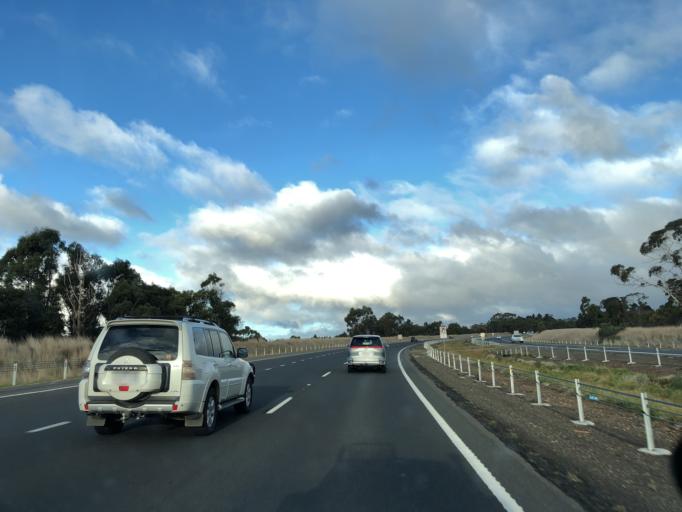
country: AU
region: Victoria
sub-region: Mount Alexander
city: Castlemaine
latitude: -37.2439
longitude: 144.4685
